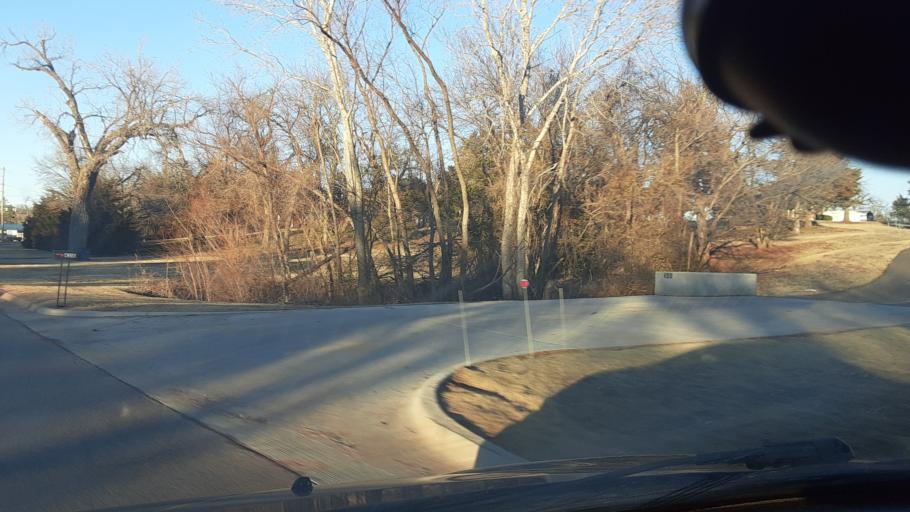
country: US
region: Oklahoma
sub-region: Logan County
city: Guthrie
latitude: 35.8342
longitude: -97.4254
